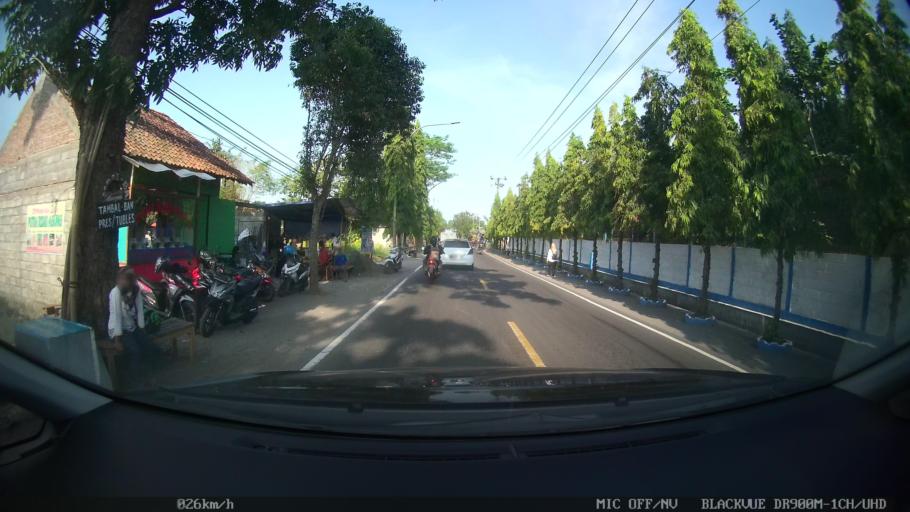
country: ID
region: Daerah Istimewa Yogyakarta
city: Bantul
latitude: -7.8768
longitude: 110.3217
